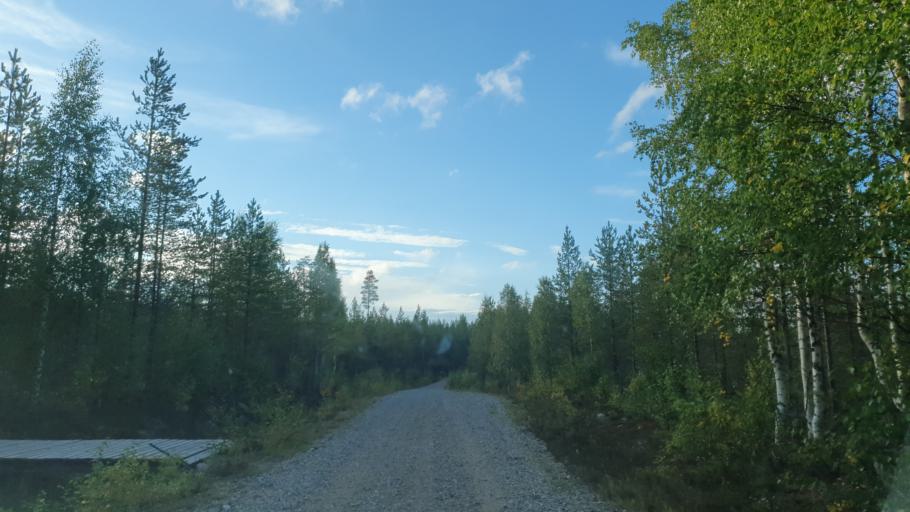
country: FI
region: Kainuu
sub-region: Kehys-Kainuu
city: Kuhmo
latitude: 64.3314
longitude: 30.0139
